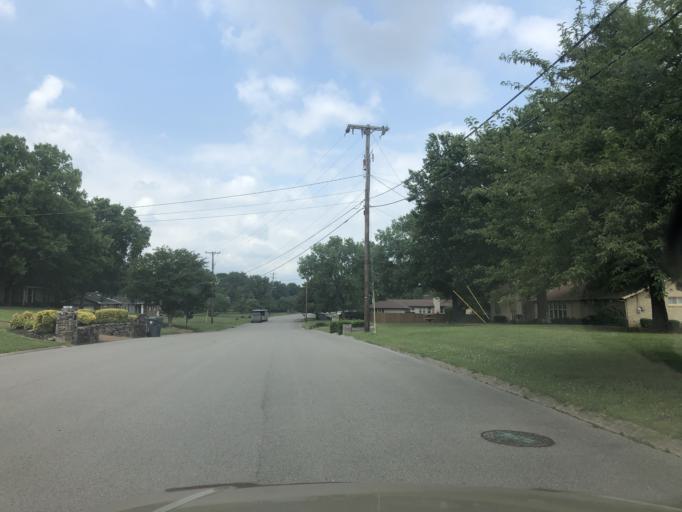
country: US
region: Tennessee
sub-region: Davidson County
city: Lakewood
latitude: 36.2350
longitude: -86.6109
